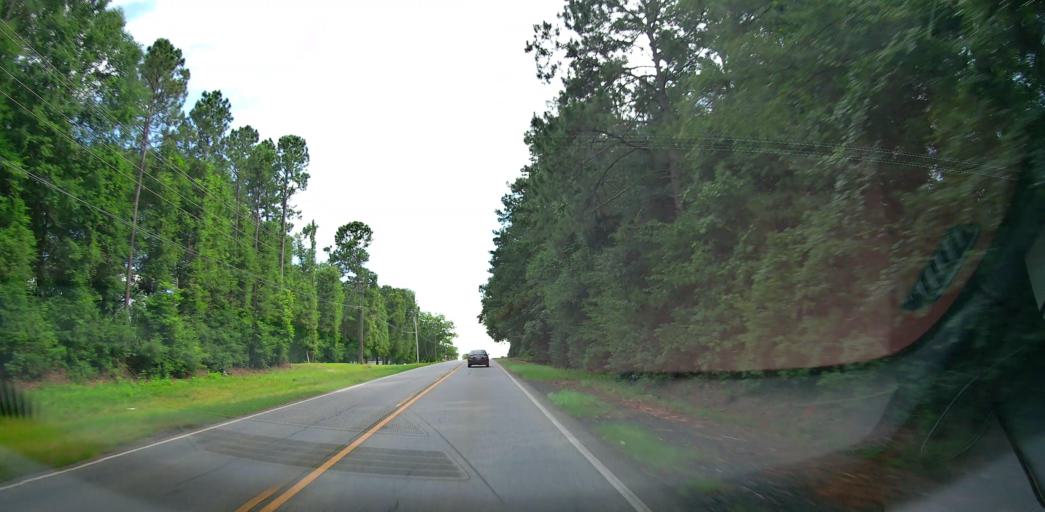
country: US
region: Georgia
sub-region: Houston County
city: Perry
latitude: 32.5168
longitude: -83.7257
